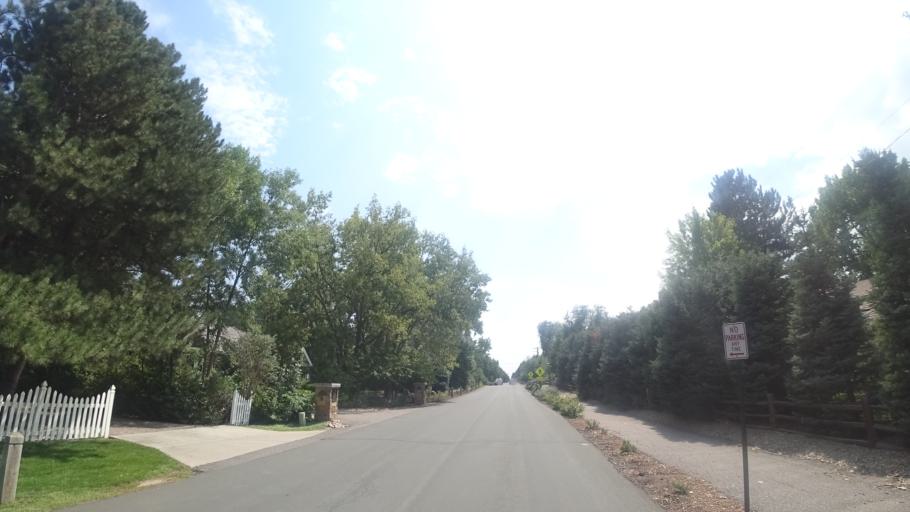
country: US
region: Colorado
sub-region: Arapahoe County
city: Greenwood Village
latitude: 39.6200
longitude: -104.9693
